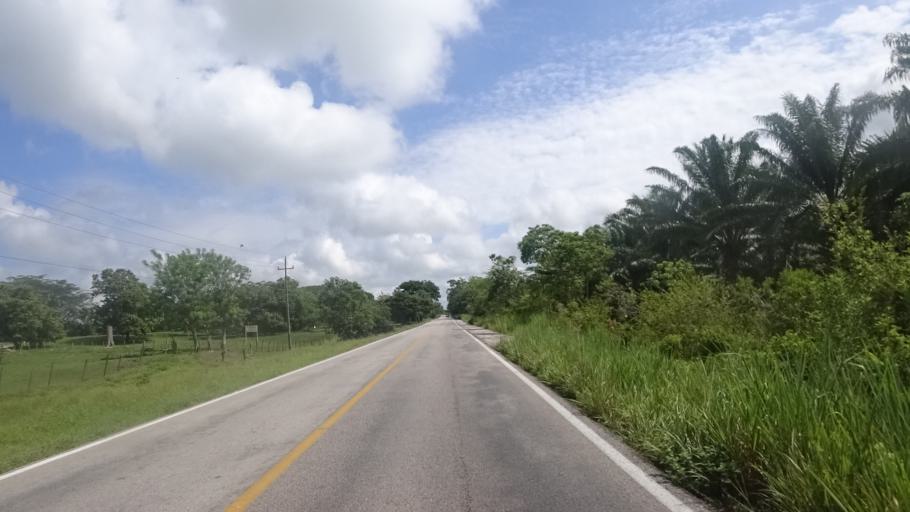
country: MX
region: Chiapas
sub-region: Catazaja
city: Catazaja
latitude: 17.6681
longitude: -92.0342
